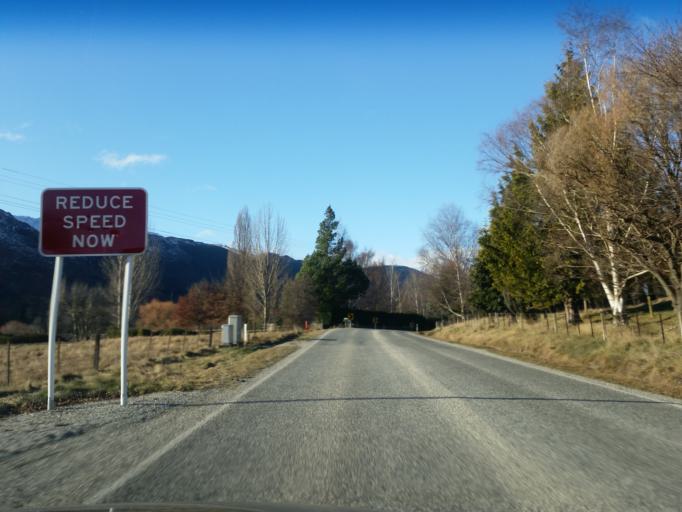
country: NZ
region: Otago
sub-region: Queenstown-Lakes District
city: Arrowtown
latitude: -44.9564
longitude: 168.7350
